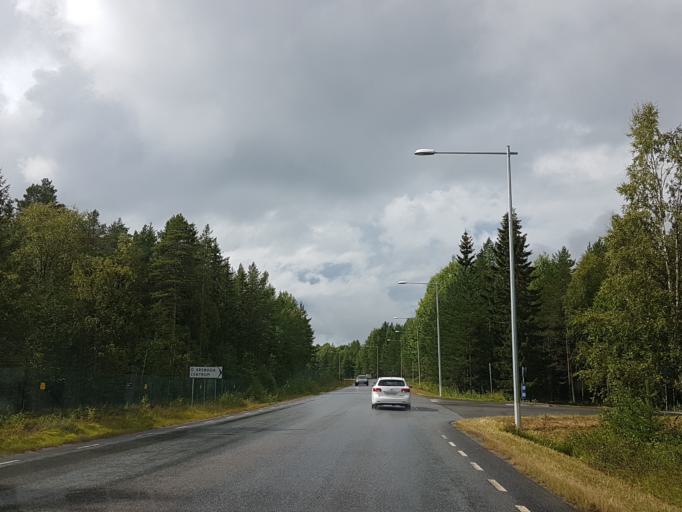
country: SE
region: Vaesterbotten
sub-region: Umea Kommun
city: Ersmark
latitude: 63.8529
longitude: 20.3400
